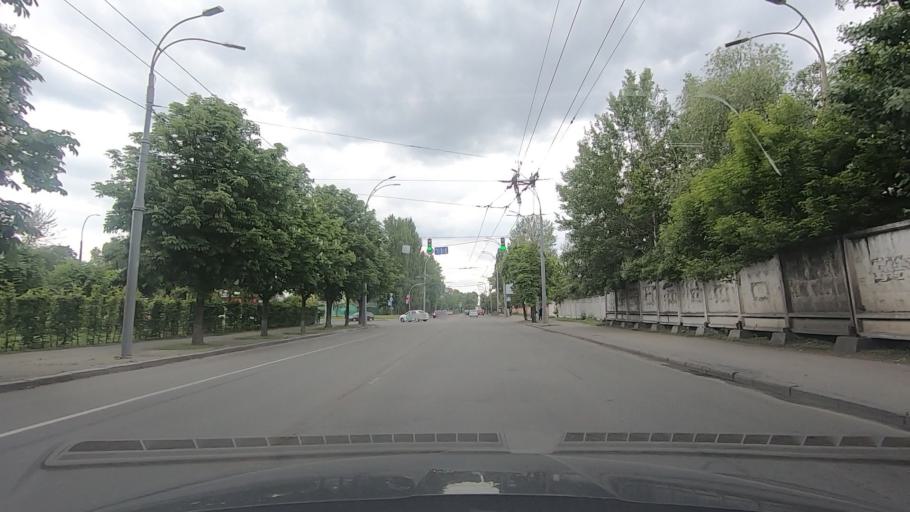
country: MD
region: Riscani
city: Riscani
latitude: 48.0512
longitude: 27.5888
